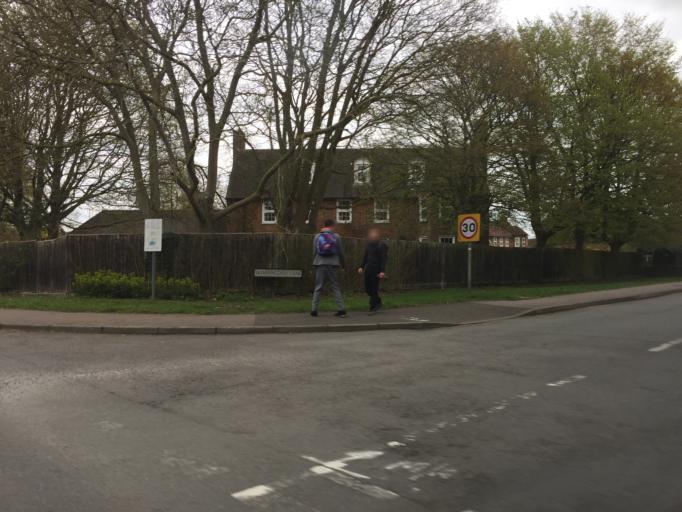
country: GB
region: England
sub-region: Oxfordshire
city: Bicester
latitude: 51.9197
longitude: -1.1503
